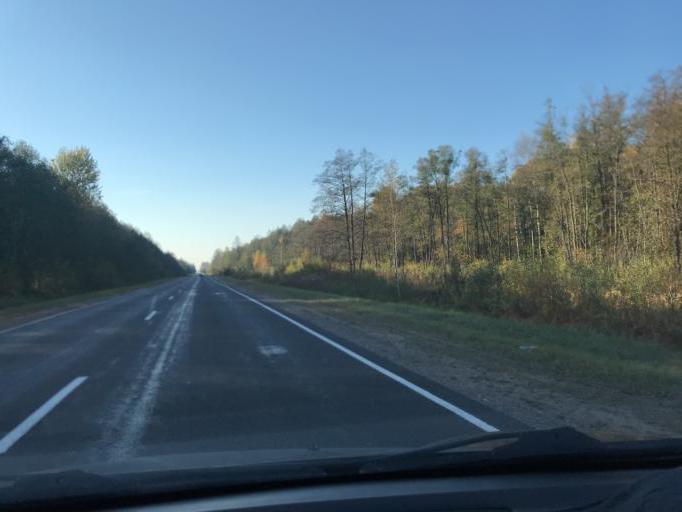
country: BY
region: Minsk
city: Staryya Darohi
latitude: 53.0420
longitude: 28.1556
